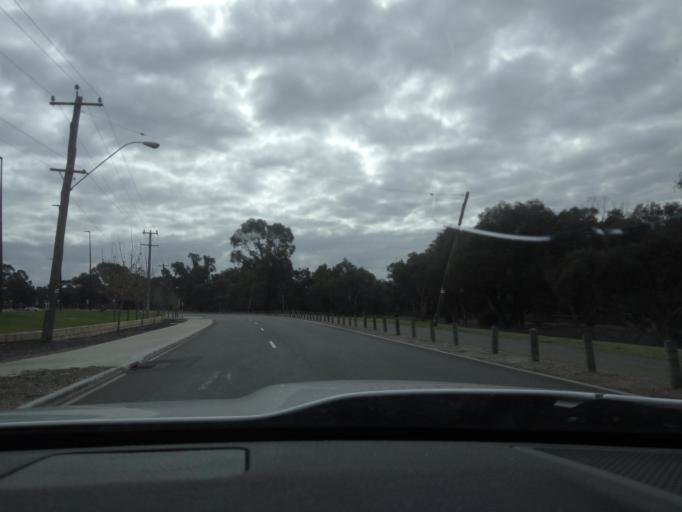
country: AU
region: Western Australia
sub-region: City of Cockburn
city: Bibra Lake
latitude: -32.0939
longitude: 115.8203
